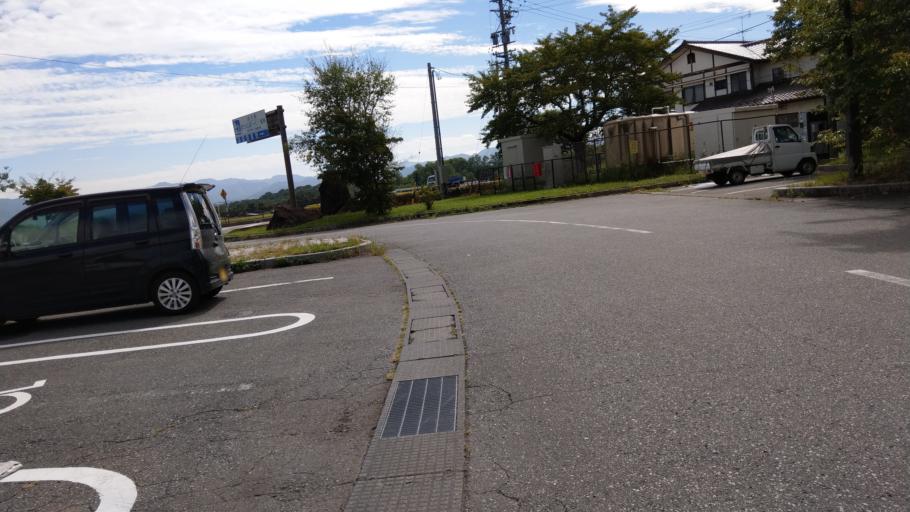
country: JP
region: Nagano
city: Komoro
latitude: 36.2573
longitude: 138.4043
